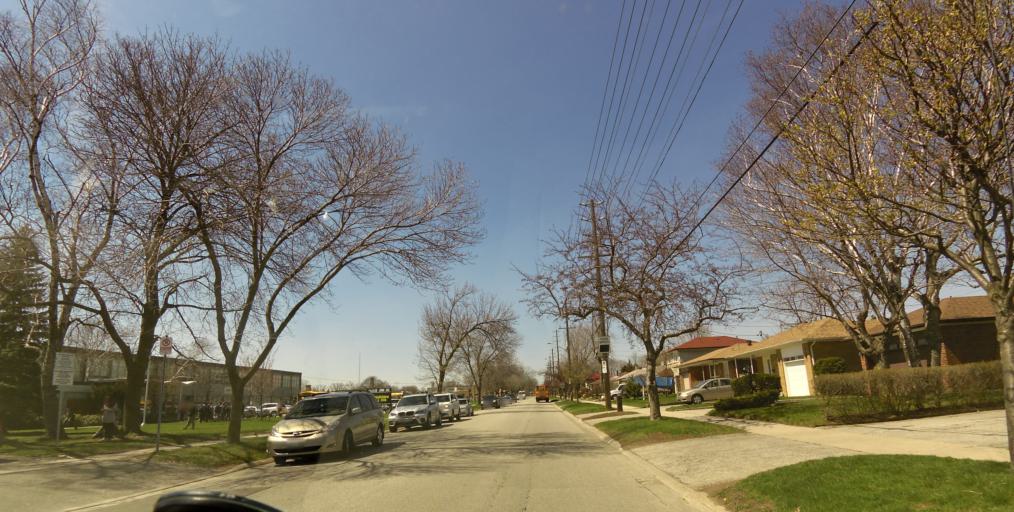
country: CA
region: Ontario
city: Etobicoke
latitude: 43.5842
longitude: -79.5687
